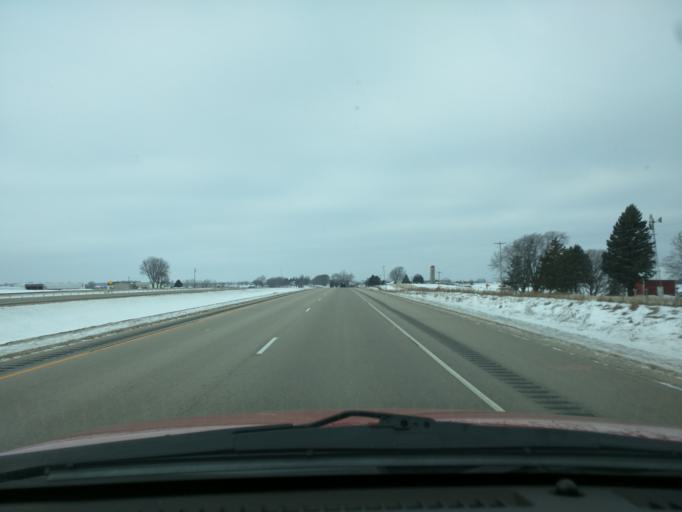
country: US
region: Wisconsin
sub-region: Trempealeau County
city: Trempealeau
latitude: 43.9253
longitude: -91.4715
